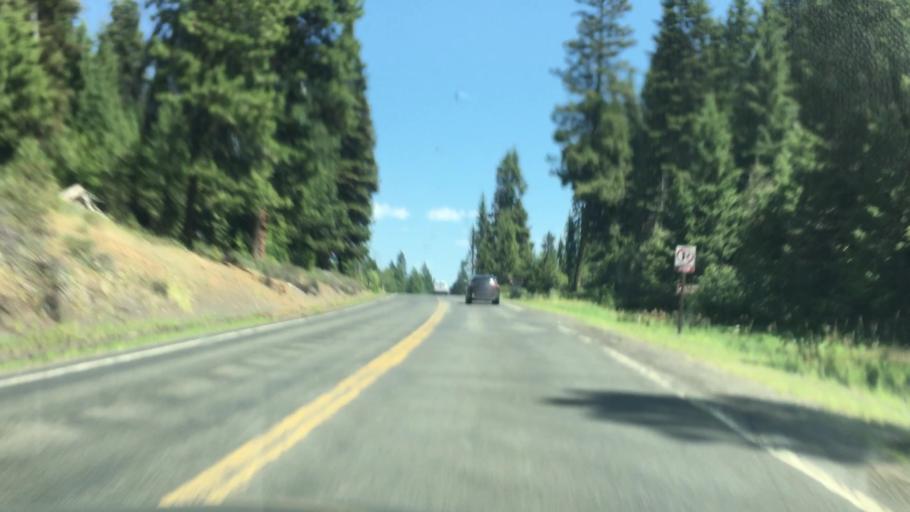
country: US
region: Idaho
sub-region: Valley County
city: McCall
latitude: 44.9298
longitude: -116.1575
